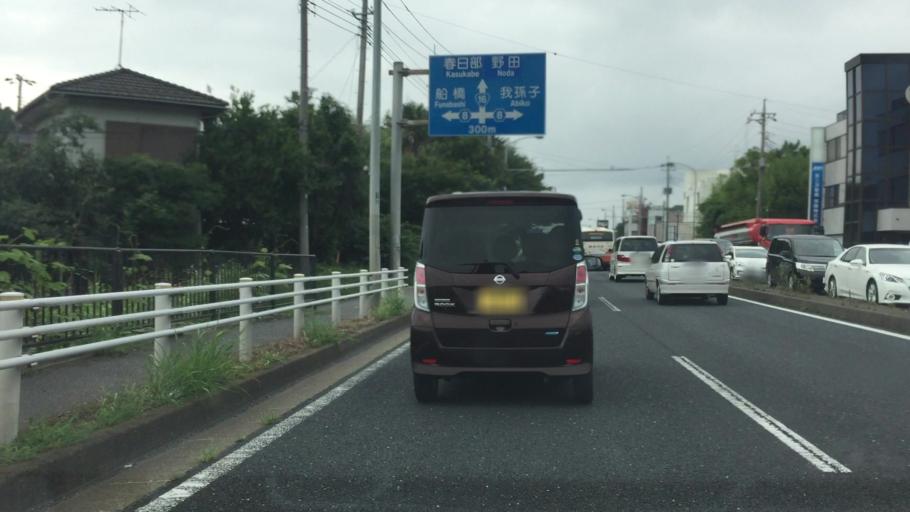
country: JP
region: Chiba
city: Abiko
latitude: 35.8348
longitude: 140.0087
